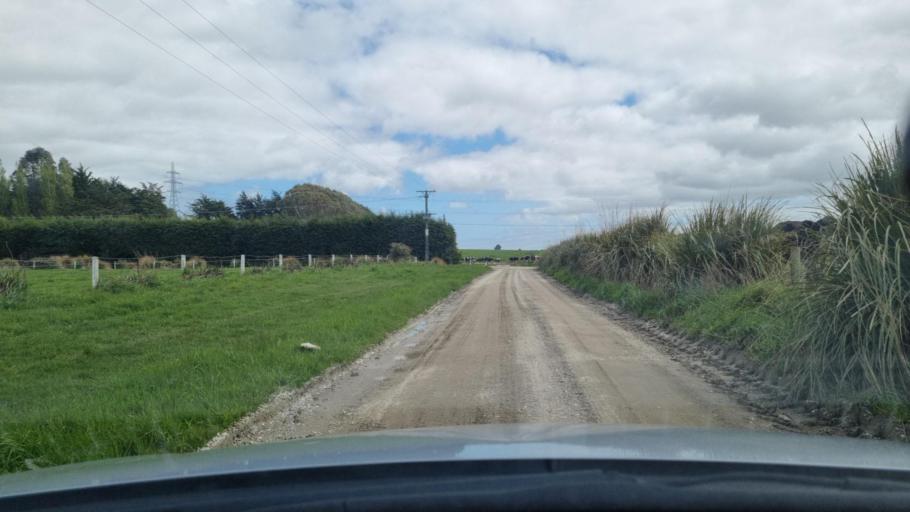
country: NZ
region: Southland
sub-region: Invercargill City
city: Invercargill
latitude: -46.4557
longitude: 168.4509
